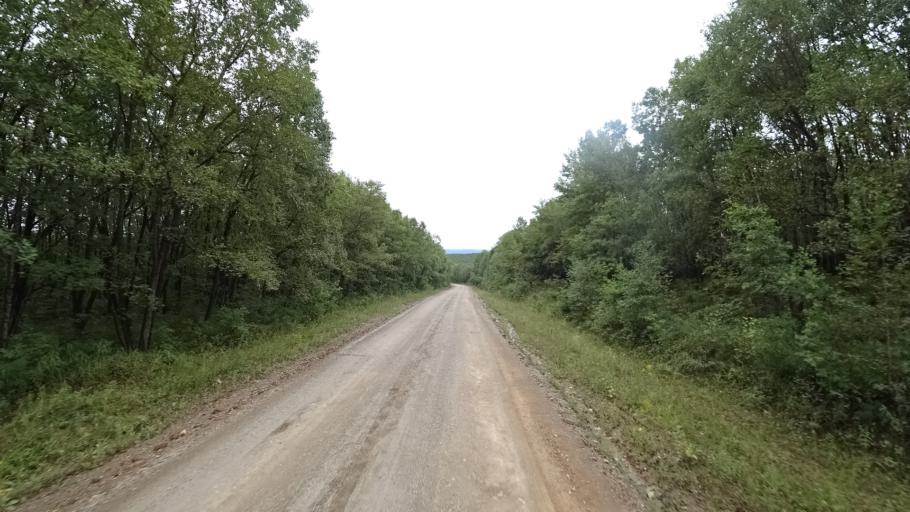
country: RU
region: Primorskiy
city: Ivanovka
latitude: 44.0337
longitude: 132.5037
